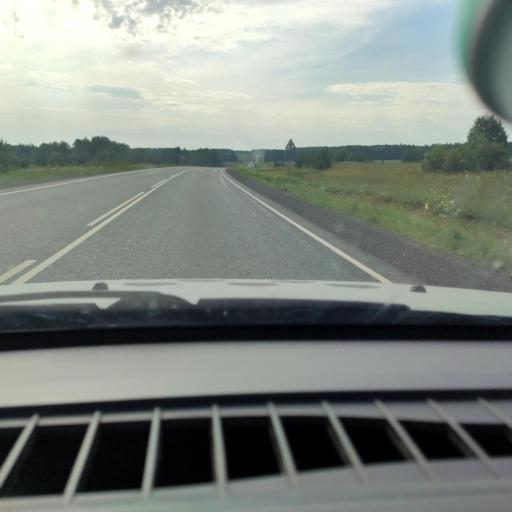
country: RU
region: Perm
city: Siva
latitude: 58.5394
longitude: 53.9602
